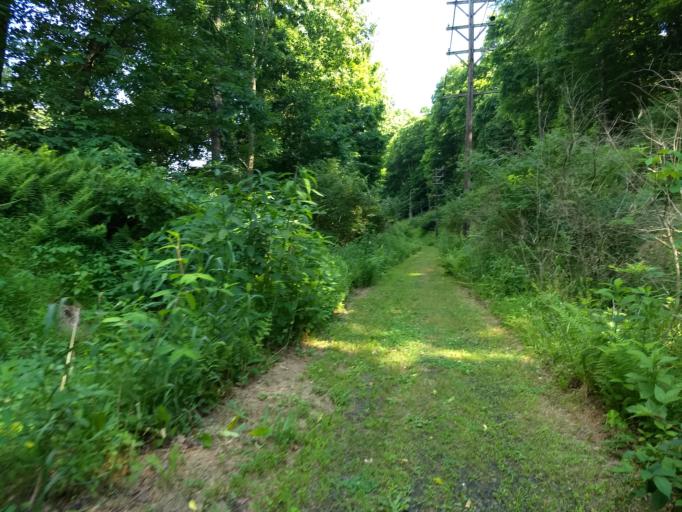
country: US
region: Pennsylvania
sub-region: Westmoreland County
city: Irwin
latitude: 40.3350
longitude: -79.7201
